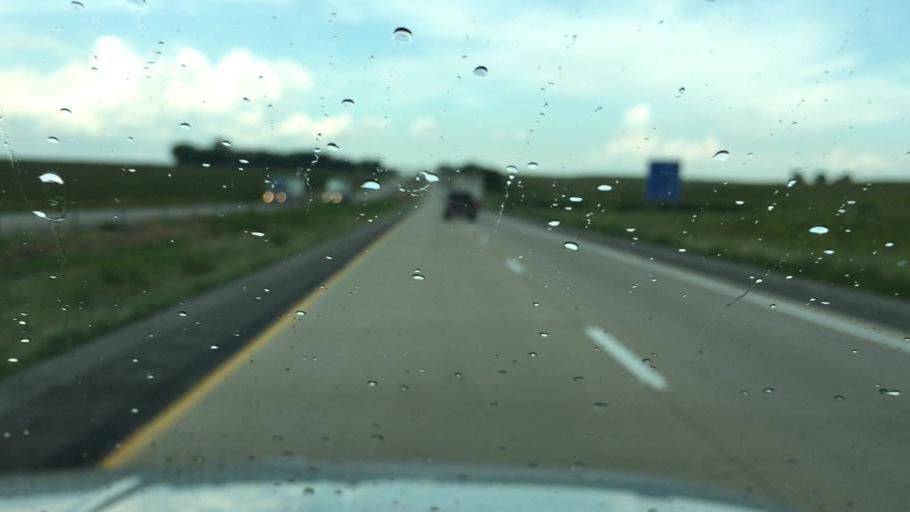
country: US
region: Iowa
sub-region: Poweshiek County
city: Brooklyn
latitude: 41.6961
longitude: -92.2536
